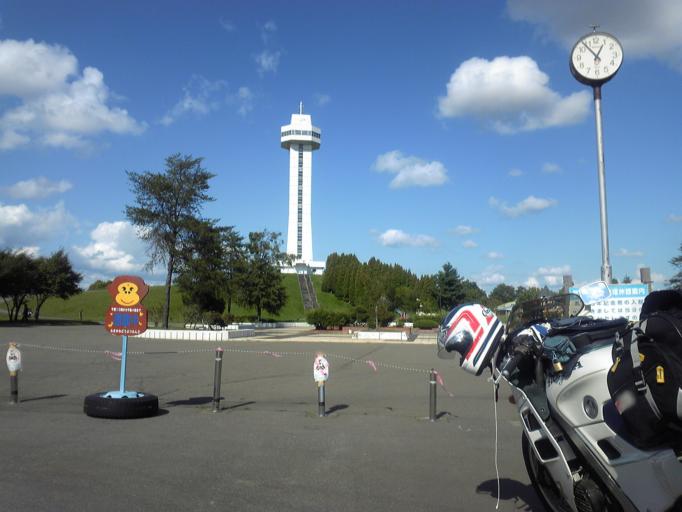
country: JP
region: Hokkaido
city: Takikawa
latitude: 43.5735
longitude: 141.8989
